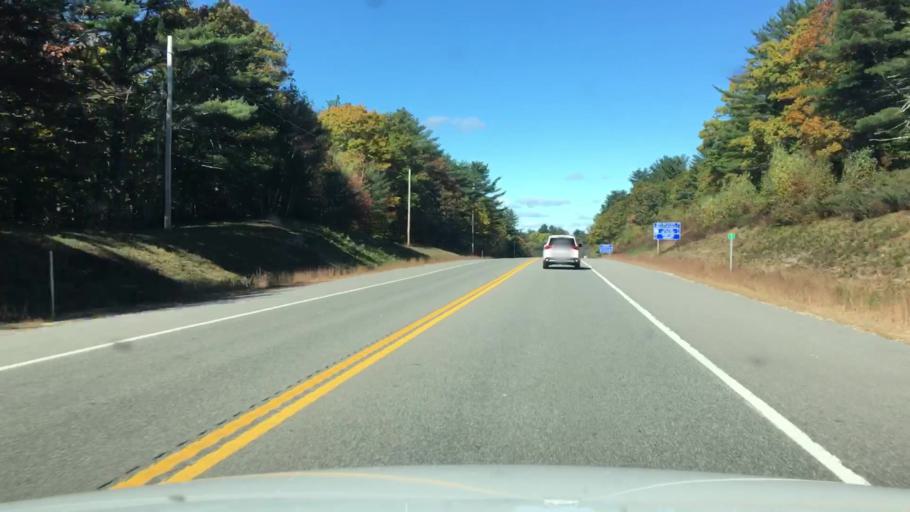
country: US
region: New Hampshire
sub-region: Carroll County
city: Sanbornville
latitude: 43.5445
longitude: -71.0361
